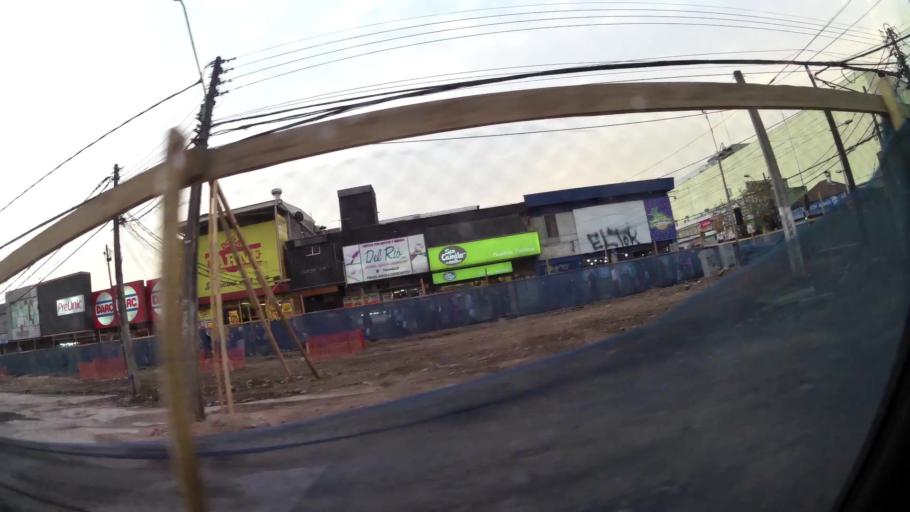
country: CL
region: Santiago Metropolitan
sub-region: Provincia de Santiago
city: Lo Prado
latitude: -33.5106
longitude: -70.7590
